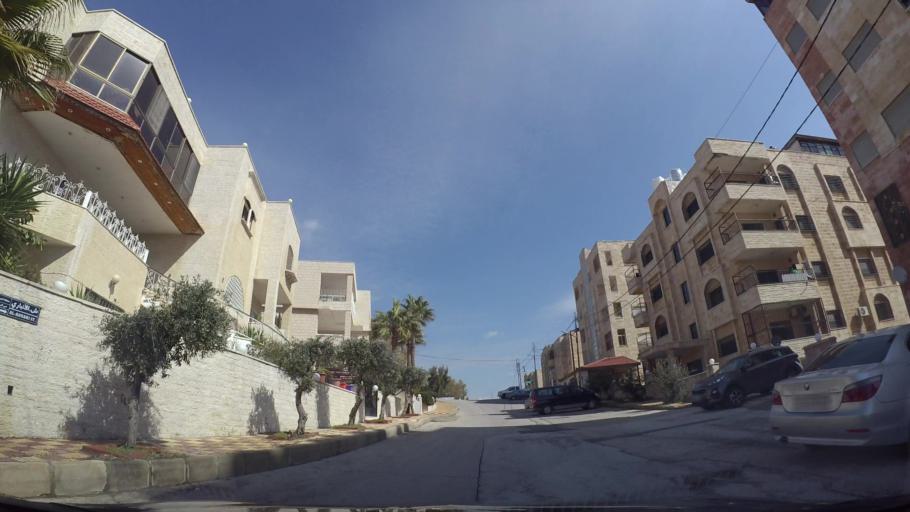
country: JO
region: Amman
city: Al Jubayhah
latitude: 31.9908
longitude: 35.8995
